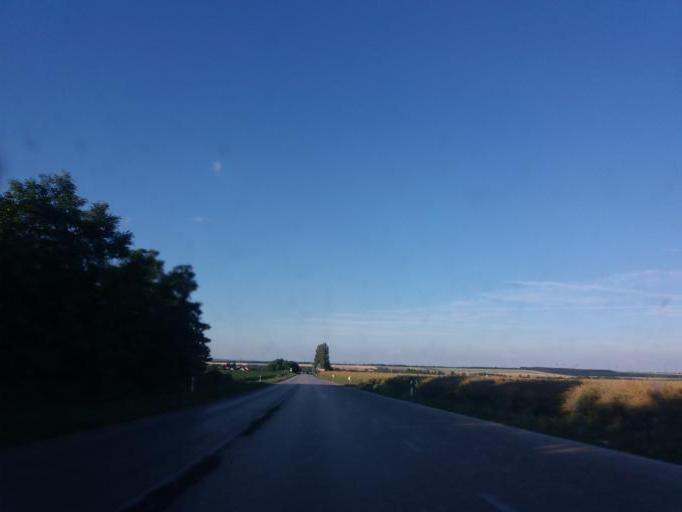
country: HU
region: Fejer
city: Baracska
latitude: 47.2997
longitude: 18.7708
